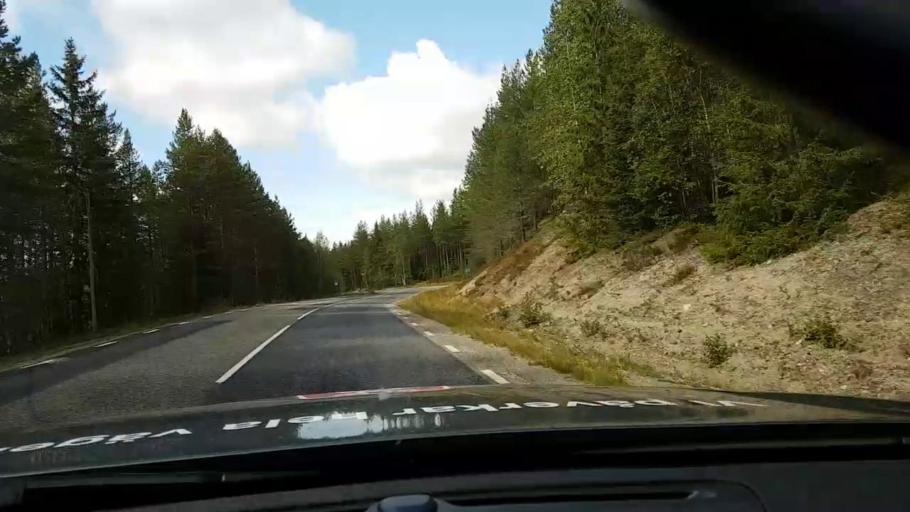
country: SE
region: Vaesterbotten
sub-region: Asele Kommun
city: Asele
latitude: 63.7951
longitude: 17.5670
